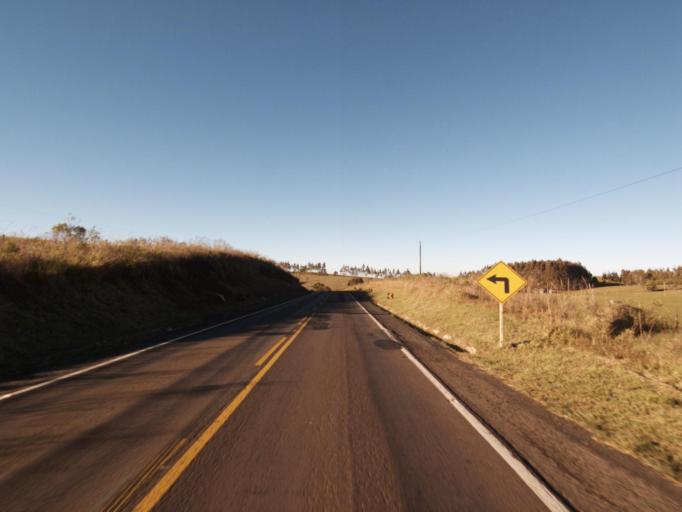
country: AR
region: Misiones
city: Bernardo de Irigoyen
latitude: -26.3015
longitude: -53.5528
